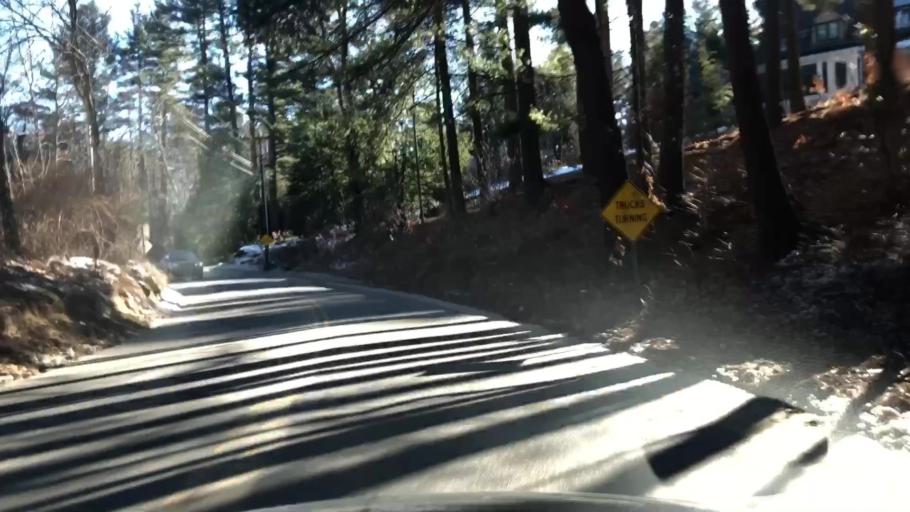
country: US
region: New Hampshire
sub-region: Hillsborough County
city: Milford
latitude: 42.8178
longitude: -71.6591
